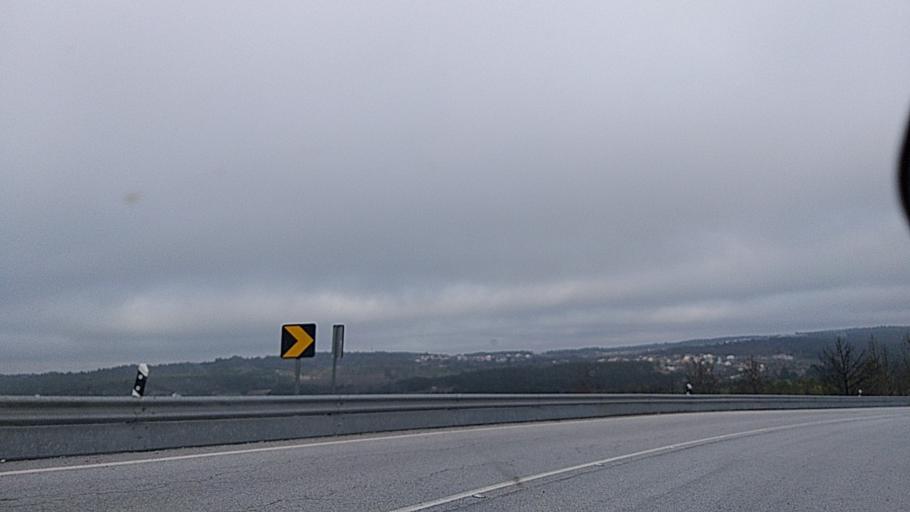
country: PT
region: Guarda
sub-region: Fornos de Algodres
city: Fornos de Algodres
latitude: 40.7083
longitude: -7.4857
